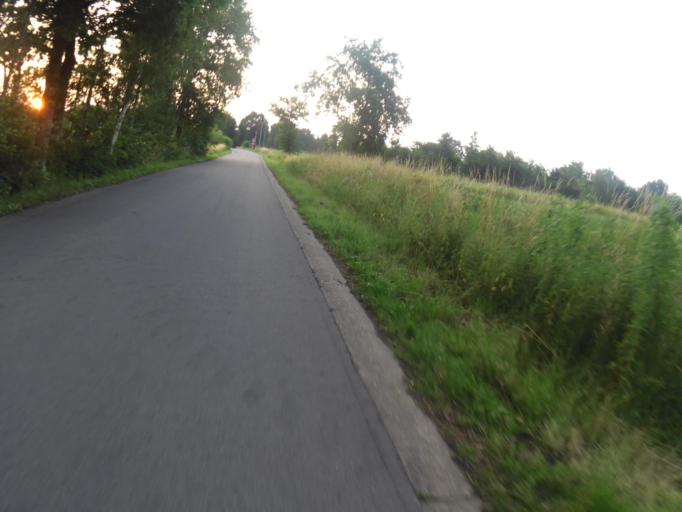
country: BE
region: Flanders
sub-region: Provincie Antwerpen
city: Meerhout
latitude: 51.1785
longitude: 5.0522
